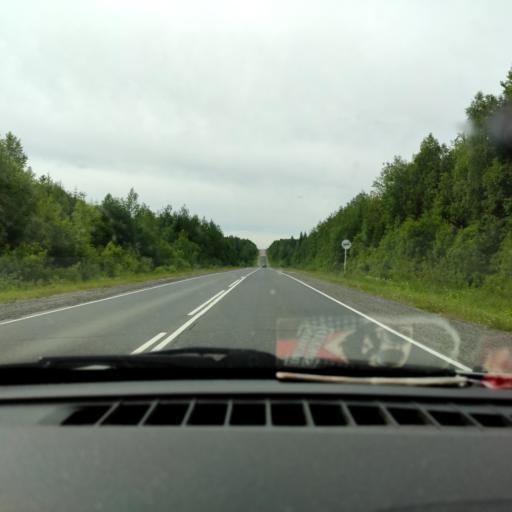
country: RU
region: Perm
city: Chusovoy
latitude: 58.3734
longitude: 57.9844
